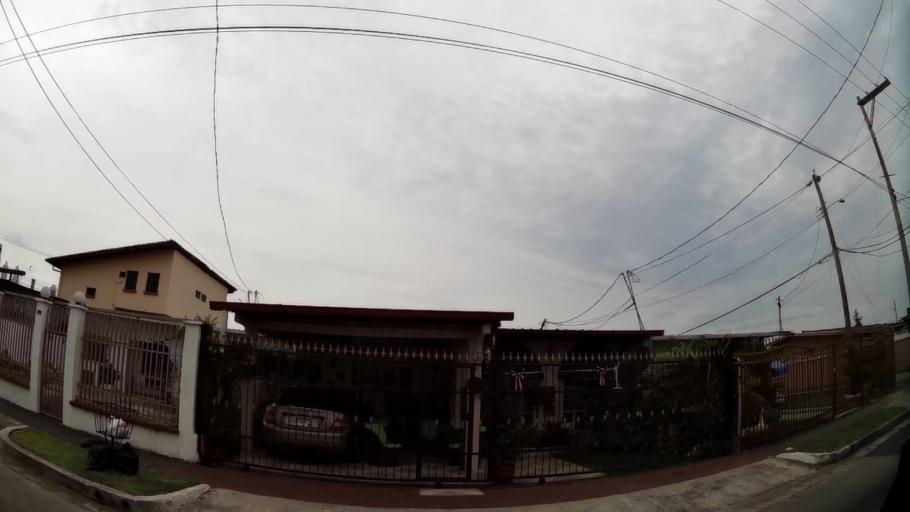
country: PA
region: Panama
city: San Miguelito
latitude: 9.0274
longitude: -79.4695
